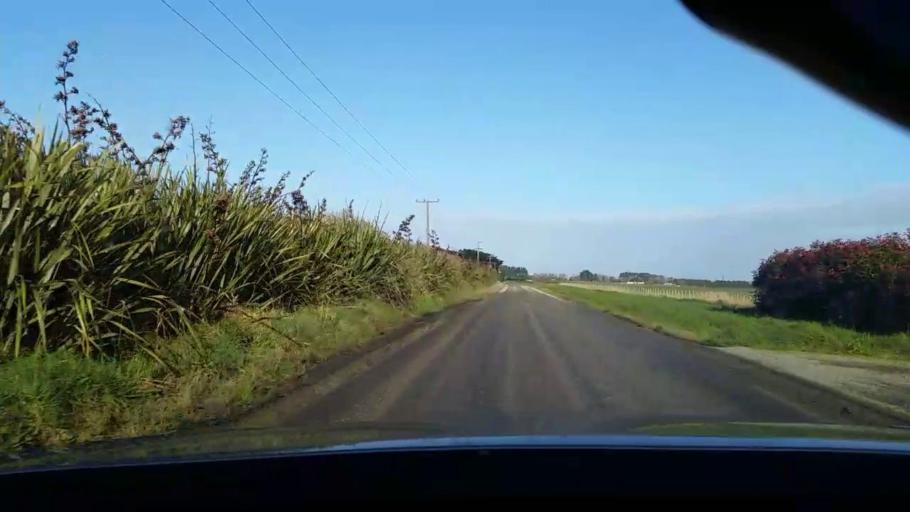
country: NZ
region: Southland
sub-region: Invercargill City
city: Invercargill
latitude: -46.3044
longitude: 168.3034
